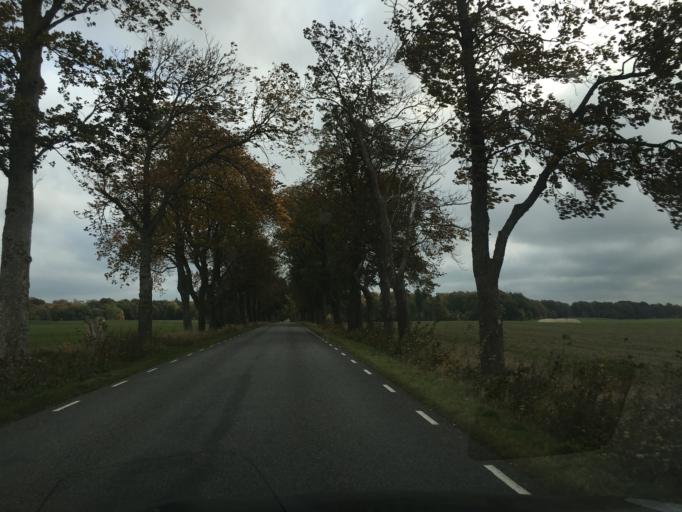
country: SE
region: Skane
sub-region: Tomelilla Kommun
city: Tomelilla
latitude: 55.6473
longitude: 14.0383
